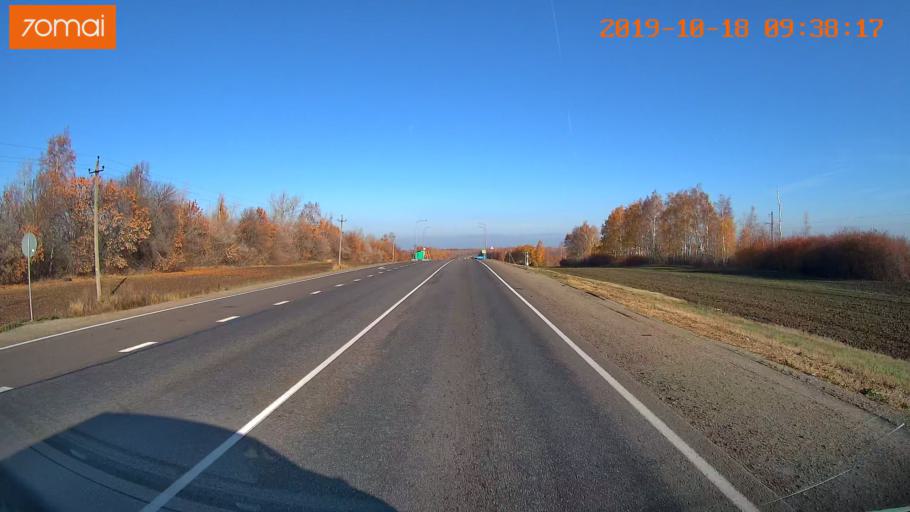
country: RU
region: Tula
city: Yefremov
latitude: 53.2357
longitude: 38.1376
